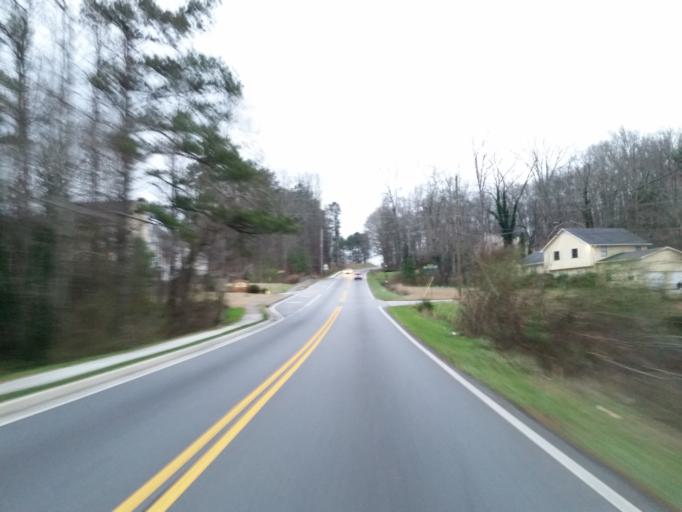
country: US
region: Georgia
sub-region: Cobb County
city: Mableton
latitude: 33.8694
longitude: -84.5782
